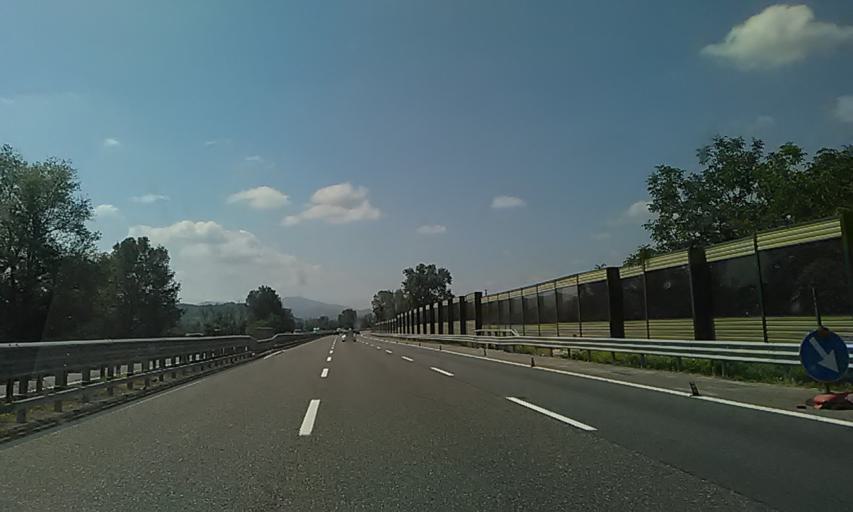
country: IT
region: Piedmont
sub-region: Provincia di Alessandria
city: Silvano d'Orba
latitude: 44.7099
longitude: 8.6671
